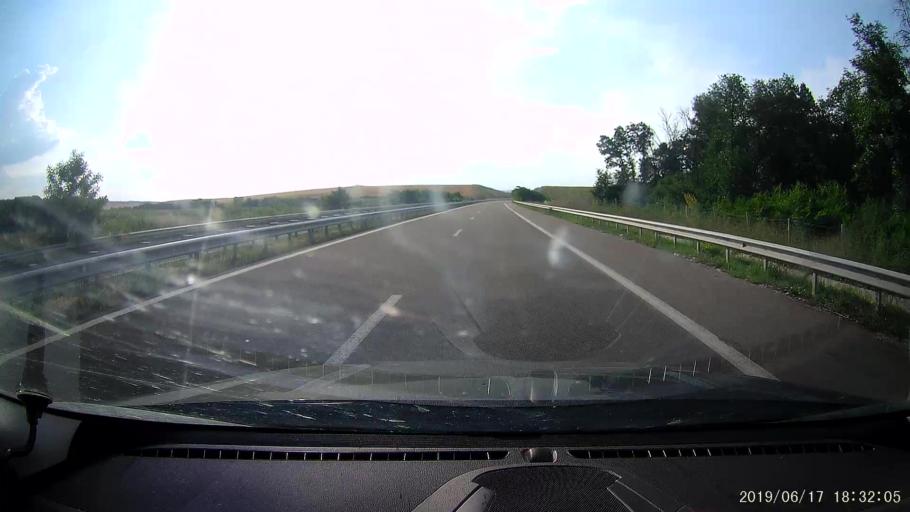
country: BG
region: Khaskovo
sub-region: Obshtina Dimitrovgrad
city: Dimitrovgrad
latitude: 42.0544
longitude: 25.4878
